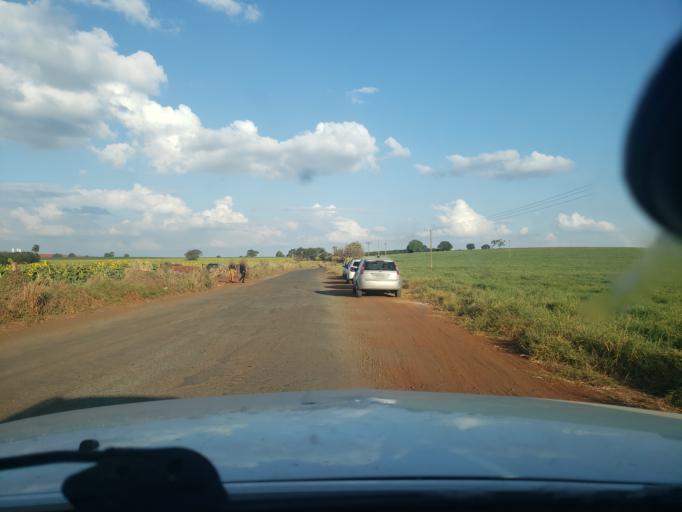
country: BR
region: Sao Paulo
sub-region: Mogi-Mirim
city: Mogi Mirim
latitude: -22.4687
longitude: -46.9306
